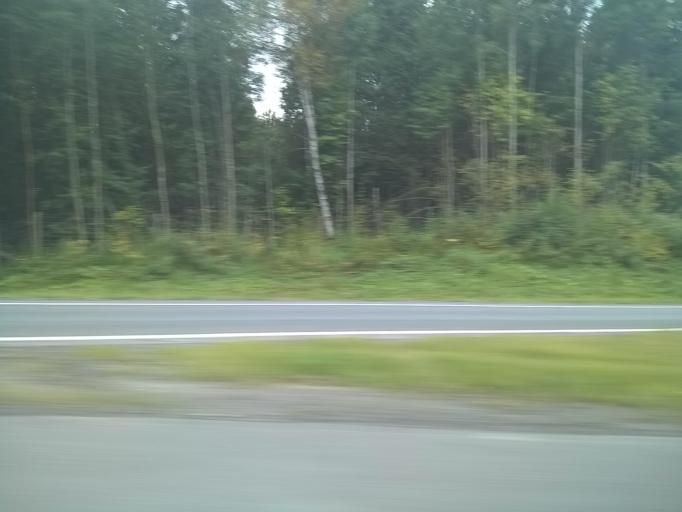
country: FI
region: Pirkanmaa
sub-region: Tampere
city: Tampere
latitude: 61.4667
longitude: 23.8410
